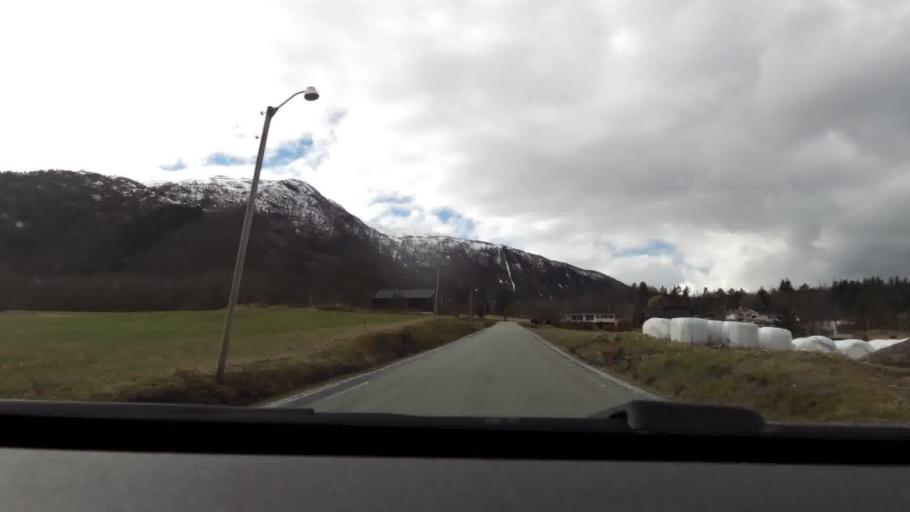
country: NO
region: More og Romsdal
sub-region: Eide
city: Eide
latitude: 62.9094
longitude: 7.5381
